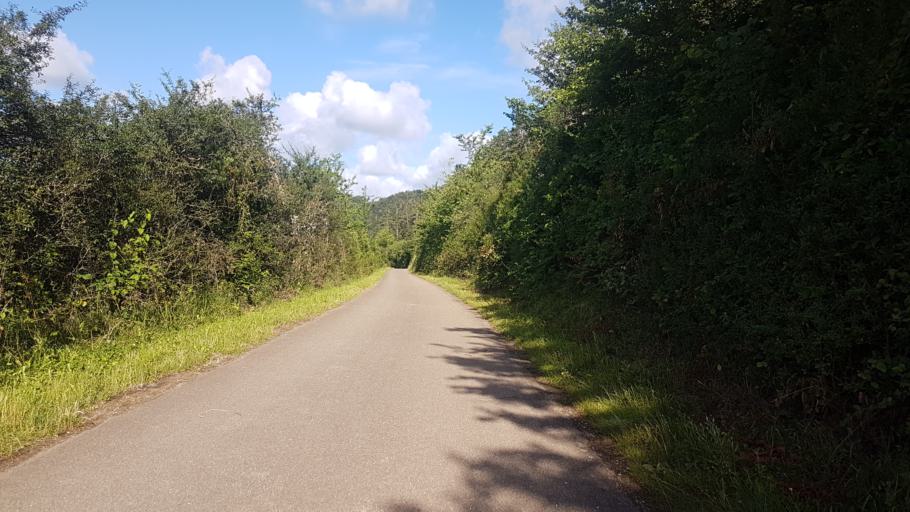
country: DE
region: Bavaria
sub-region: Upper Bavaria
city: Denkendorf
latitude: 48.9496
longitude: 11.3726
